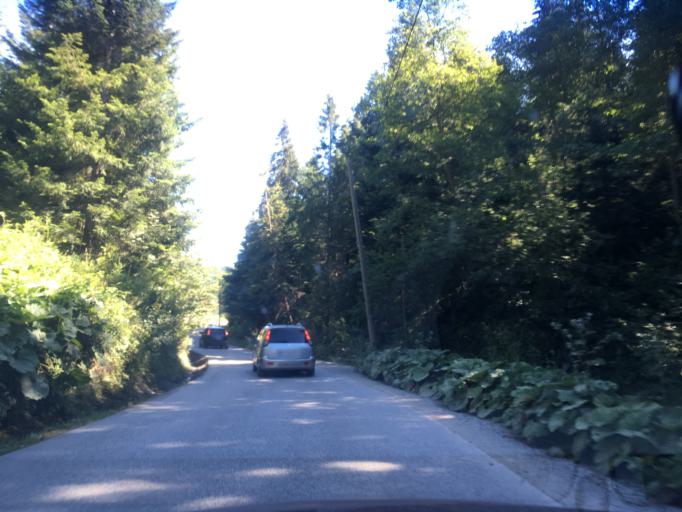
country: SK
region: Presovsky
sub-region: Okres Poprad
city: Zdiar
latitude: 49.2688
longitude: 20.3069
